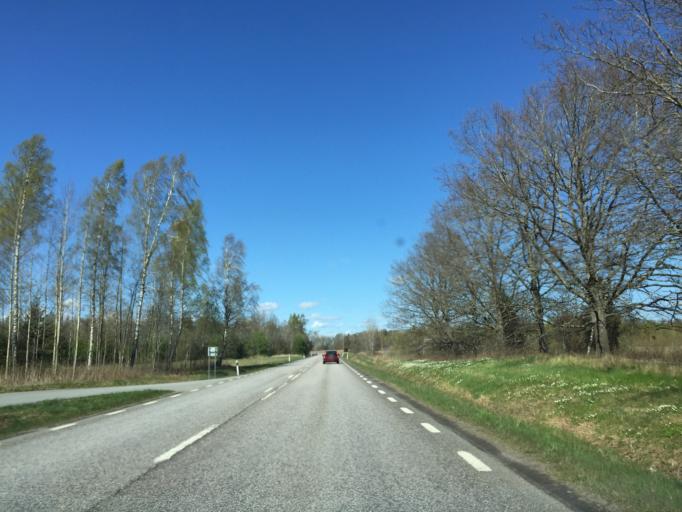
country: SE
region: OErebro
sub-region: Hallsbergs Kommun
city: Skollersta
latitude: 59.1514
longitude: 15.2679
